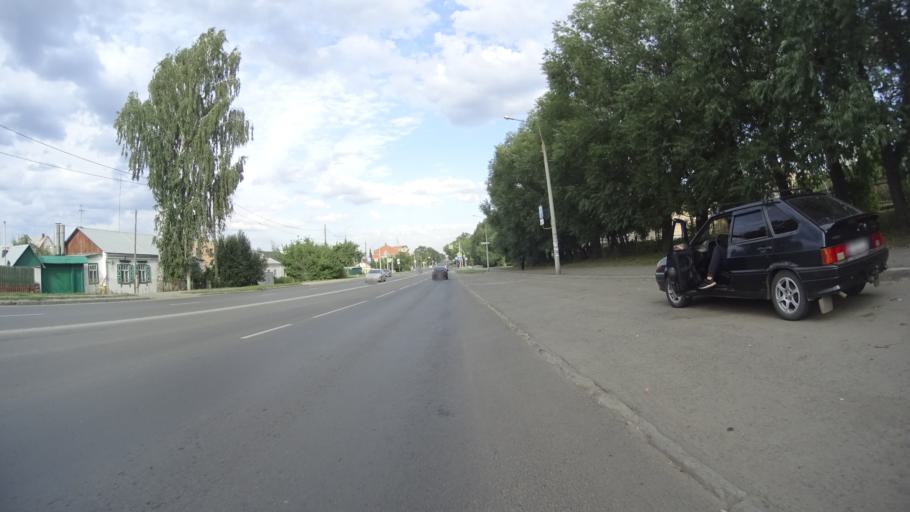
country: RU
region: Chelyabinsk
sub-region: Gorod Chelyabinsk
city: Chelyabinsk
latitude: 55.1985
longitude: 61.3398
